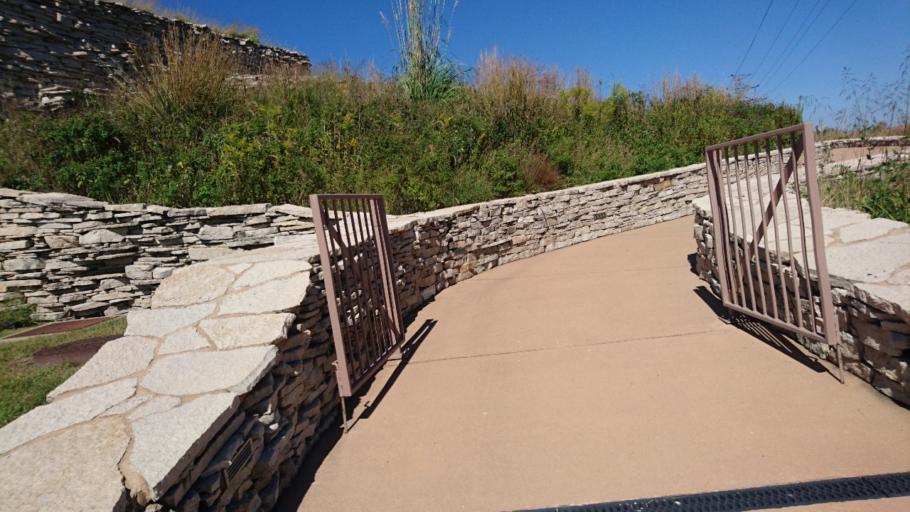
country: US
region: Illinois
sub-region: Madison County
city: East Alton
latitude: 38.8662
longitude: -90.1400
